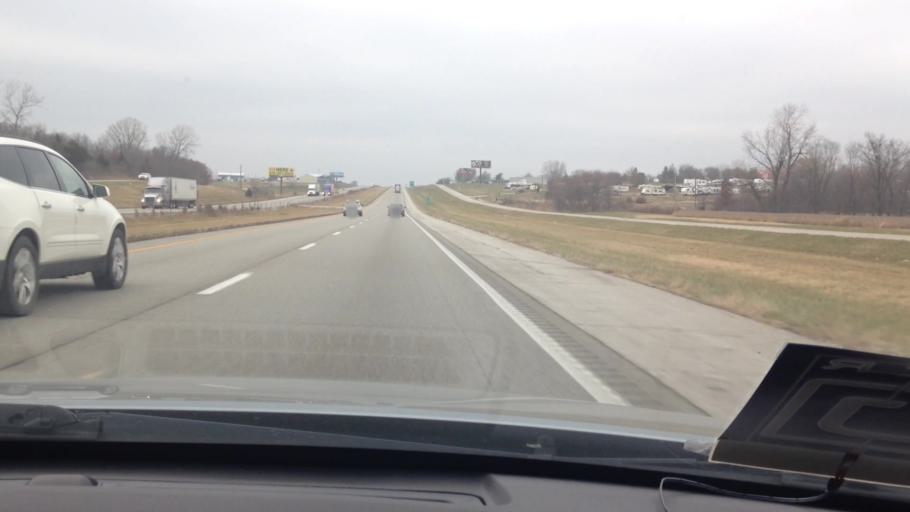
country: US
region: Missouri
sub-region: Cass County
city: Peculiar
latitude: 38.7024
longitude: -94.4354
